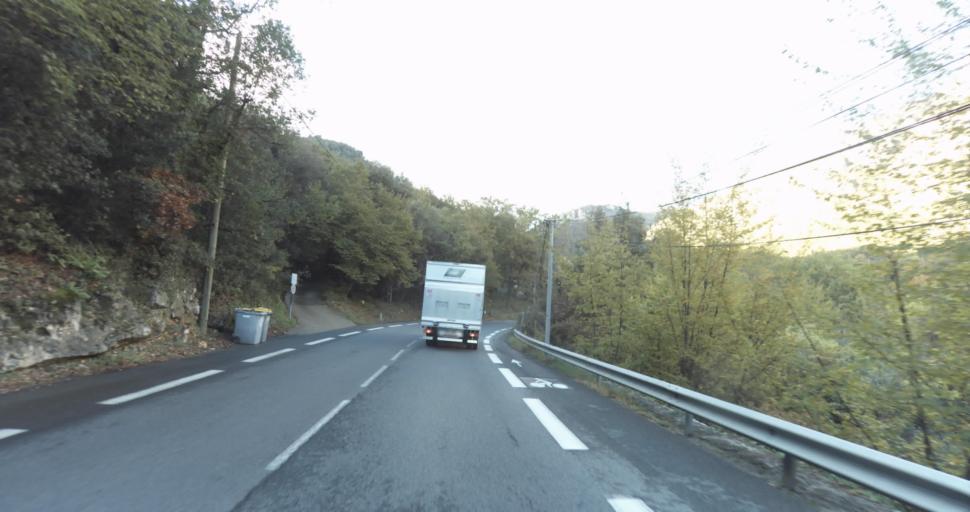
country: FR
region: Provence-Alpes-Cote d'Azur
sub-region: Departement des Alpes-Maritimes
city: Saint-Jeannet
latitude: 43.7467
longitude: 7.1307
